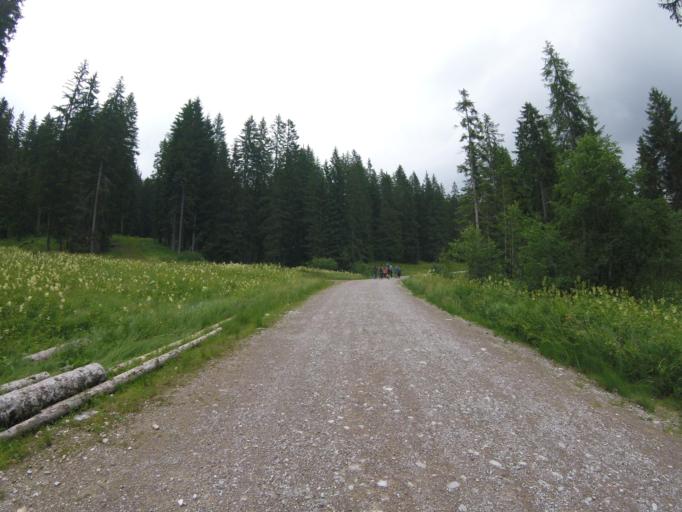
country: AT
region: Tyrol
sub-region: Politischer Bezirk Kitzbuhel
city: Waidring
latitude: 47.6560
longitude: 12.5931
